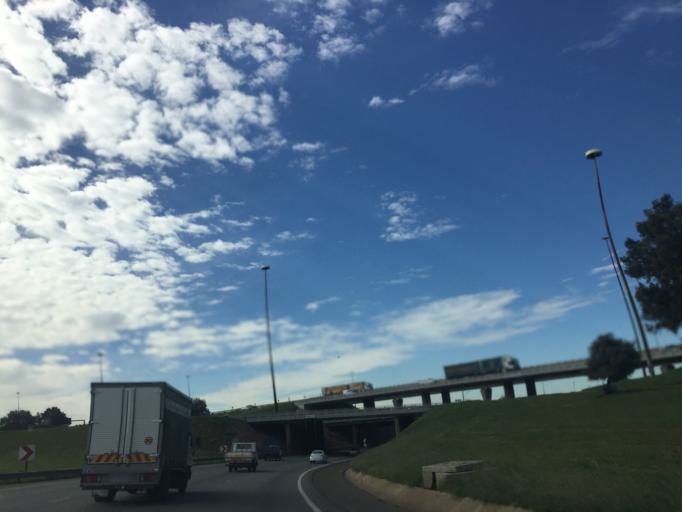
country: ZA
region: Gauteng
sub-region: Ekurhuleni Metropolitan Municipality
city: Germiston
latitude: -26.2386
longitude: 28.1264
